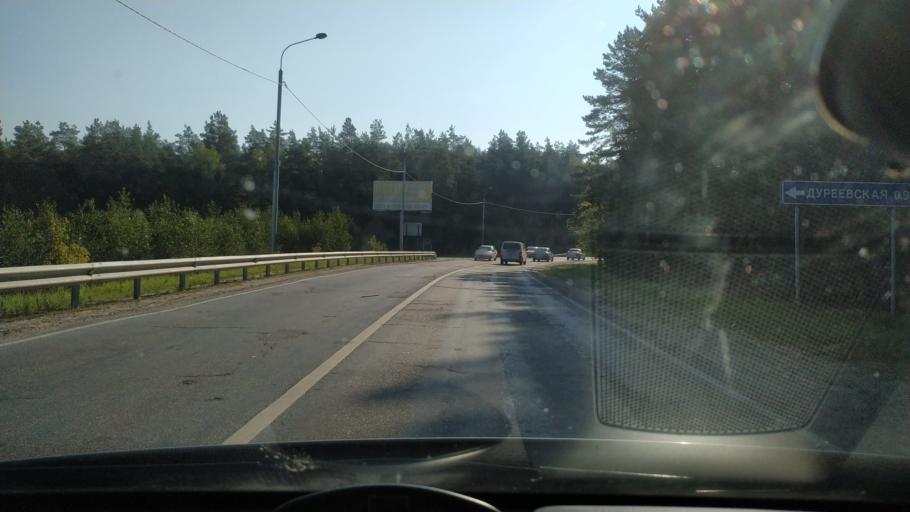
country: RU
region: Moskovskaya
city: Tugolesskiy Bor
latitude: 55.5617
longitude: 39.6995
